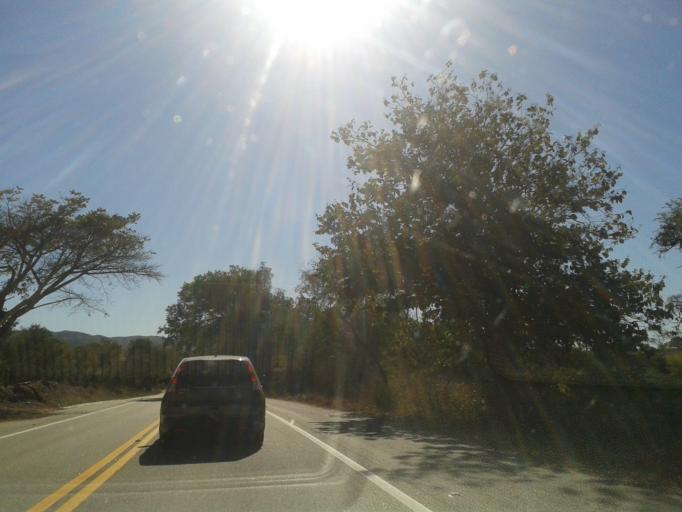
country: BR
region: Goias
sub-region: Itapuranga
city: Itapuranga
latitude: -15.5864
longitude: -50.2629
